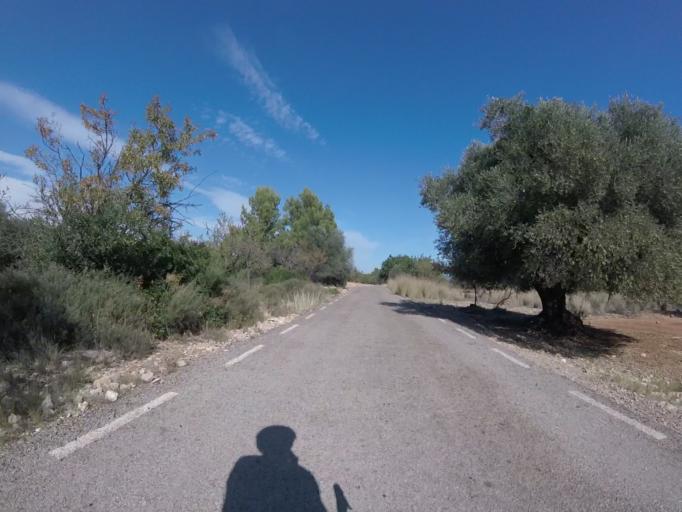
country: ES
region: Valencia
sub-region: Provincia de Castello
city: Sarratella
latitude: 40.2732
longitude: 0.0601
